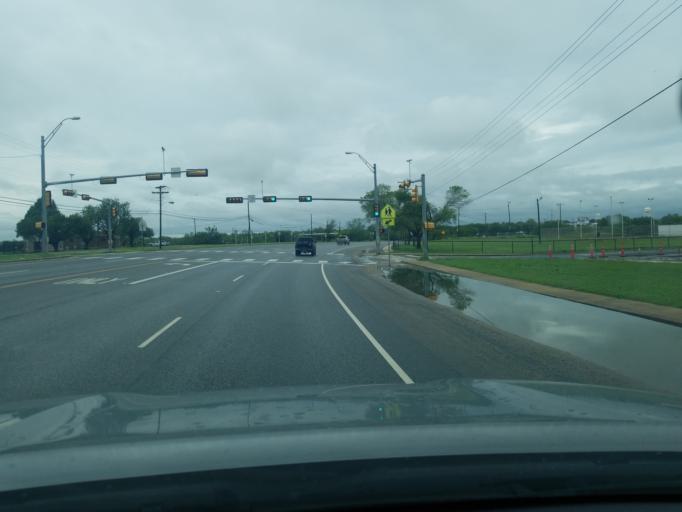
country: US
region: Texas
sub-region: Dimmit County
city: Carrizo Springs
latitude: 28.5208
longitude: -99.8470
